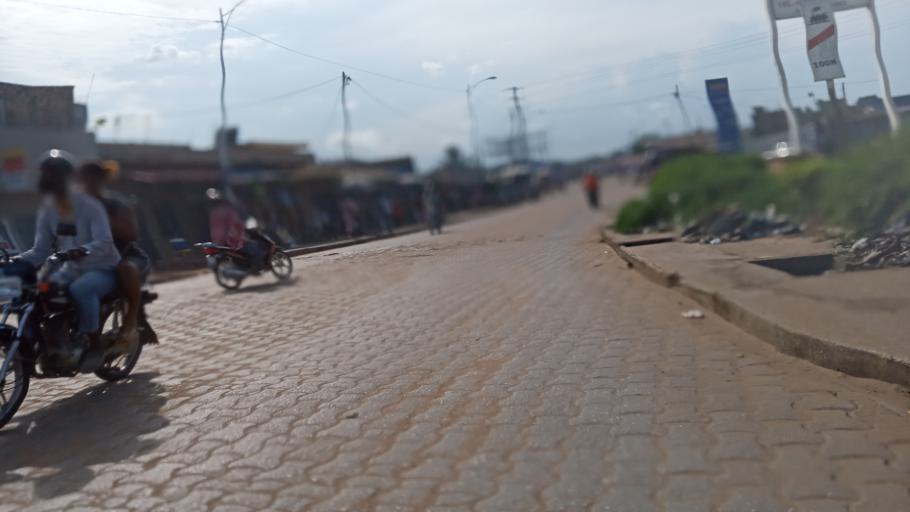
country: TG
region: Maritime
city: Lome
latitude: 6.1554
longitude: 1.2675
